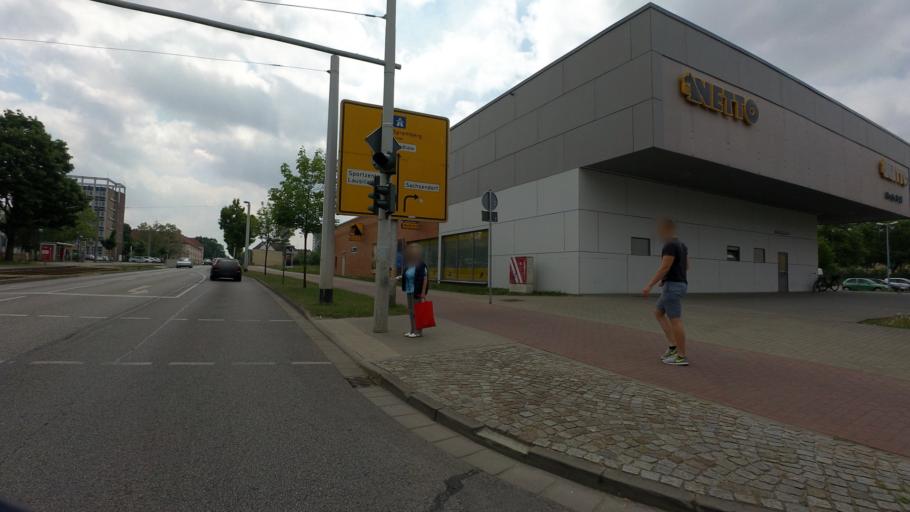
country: DE
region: Brandenburg
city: Cottbus
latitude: 51.7413
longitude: 14.3336
